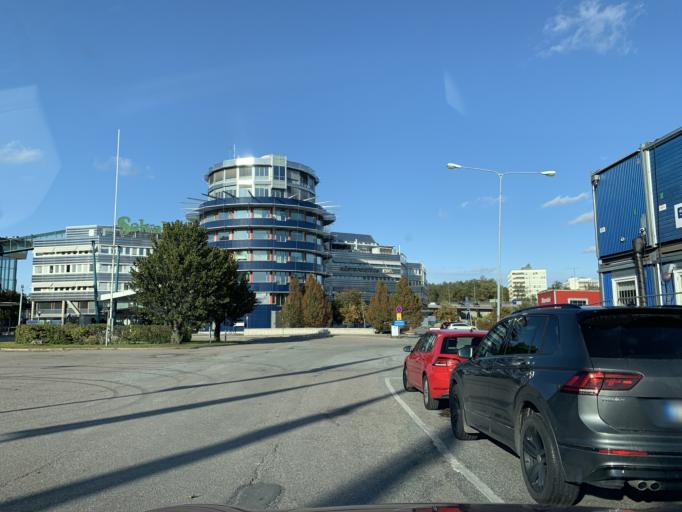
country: SE
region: Stockholm
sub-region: Stockholms Kommun
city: Bromma
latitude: 59.3648
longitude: 17.9425
